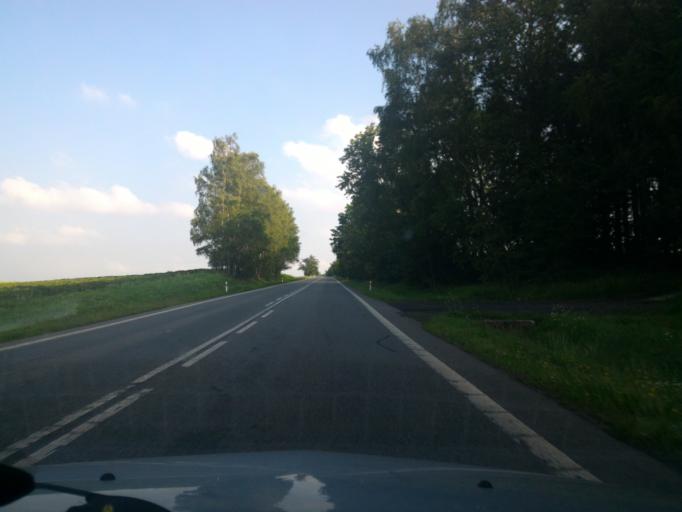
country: CZ
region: Vysocina
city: Okrouhlice
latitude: 49.6732
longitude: 15.5389
